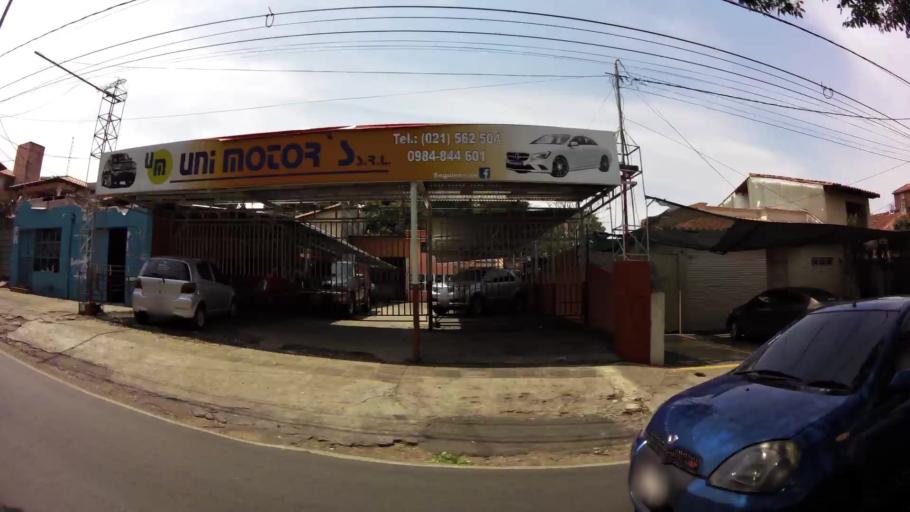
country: PY
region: Central
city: Lambare
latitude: -25.3210
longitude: -57.5937
